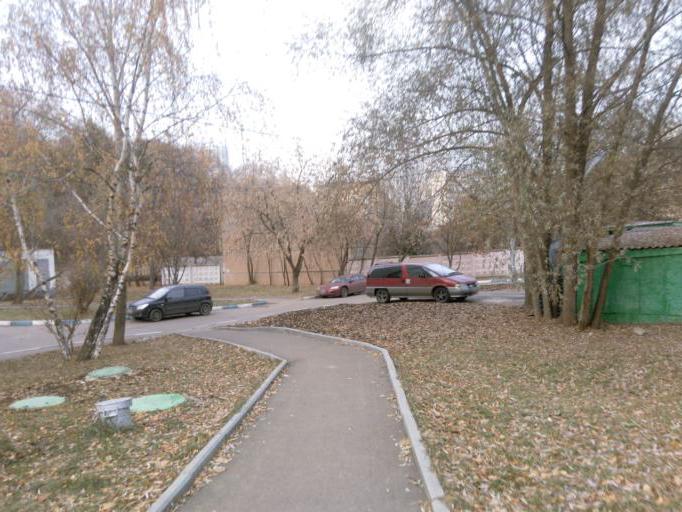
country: RU
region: Moscow
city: Troparevo
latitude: 55.6544
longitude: 37.5142
